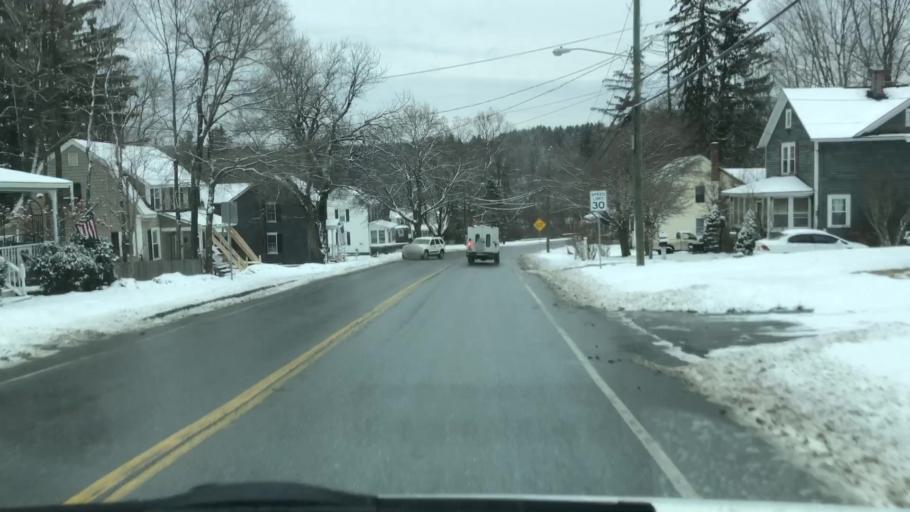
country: US
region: Massachusetts
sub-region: Berkshire County
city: Dalton
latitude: 42.4671
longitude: -73.1820
